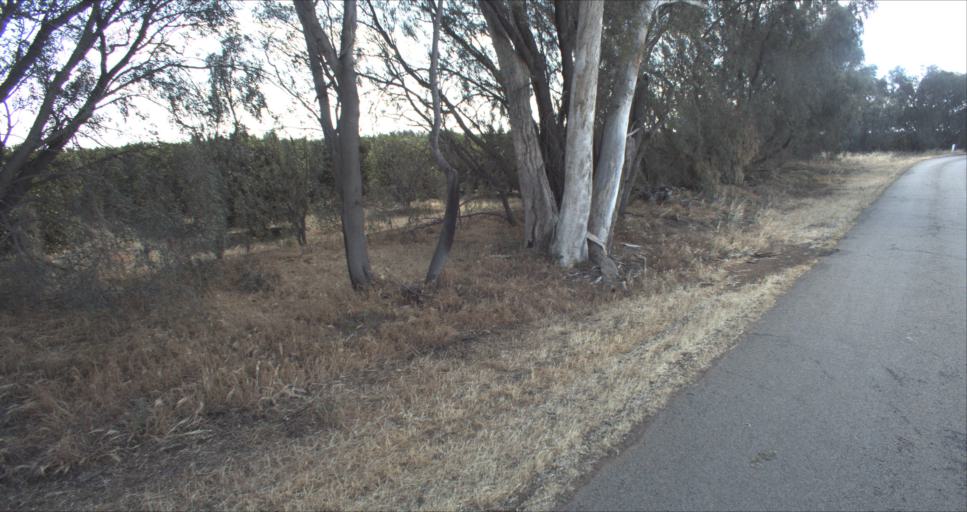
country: AU
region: New South Wales
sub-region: Leeton
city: Leeton
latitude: -34.5122
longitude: 146.2322
